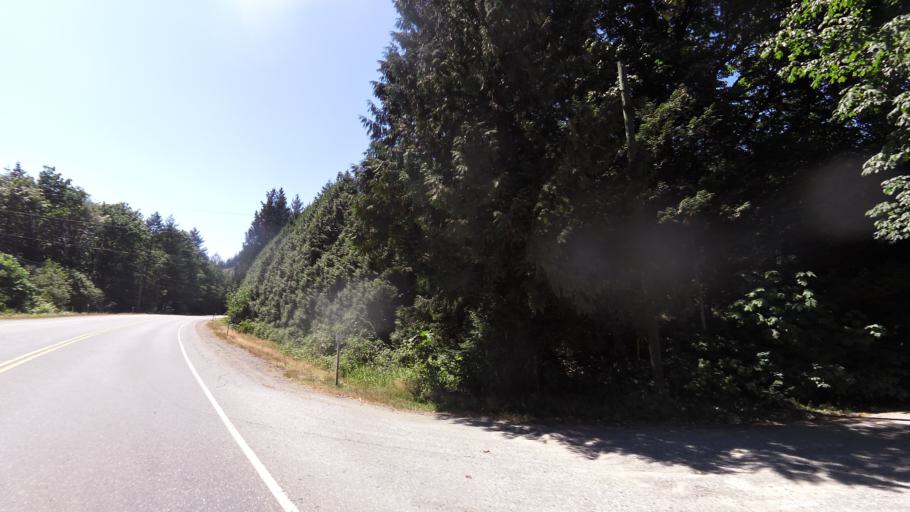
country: CA
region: British Columbia
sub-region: Fraser Valley Regional District
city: Chilliwack
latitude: 49.2325
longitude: -122.0086
